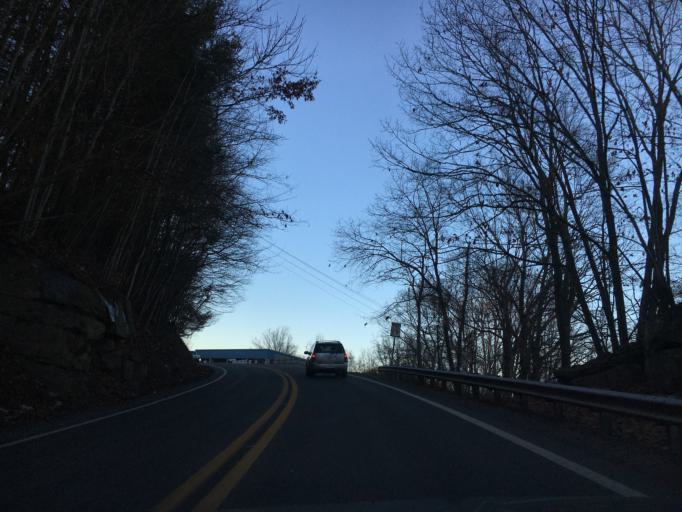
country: US
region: West Virginia
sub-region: Raleigh County
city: Beaver
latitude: 37.7655
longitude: -81.1567
